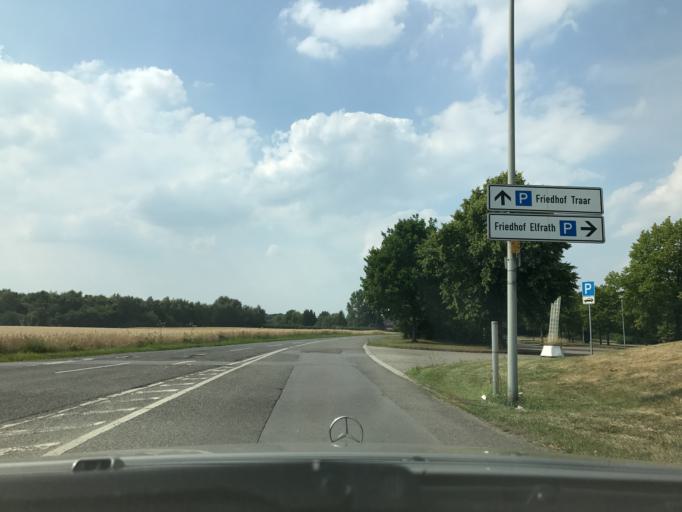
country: DE
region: North Rhine-Westphalia
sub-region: Regierungsbezirk Dusseldorf
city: Krefeld
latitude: 51.3736
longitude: 6.6146
